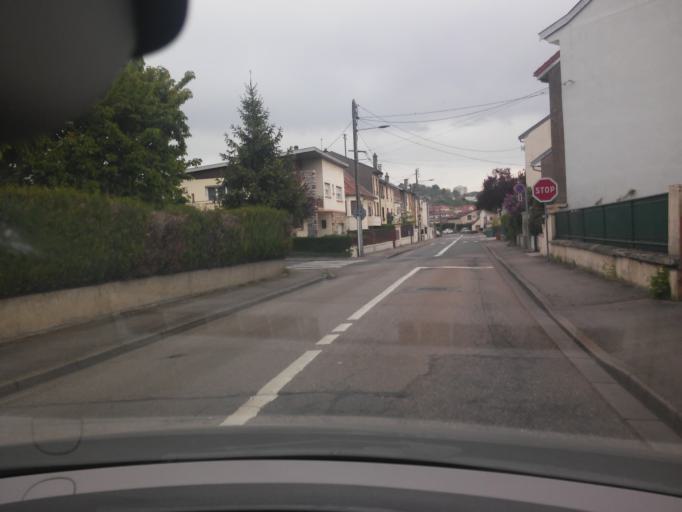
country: FR
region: Lorraine
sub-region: Departement de Meurthe-et-Moselle
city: Laxou
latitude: 48.6801
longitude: 6.1434
